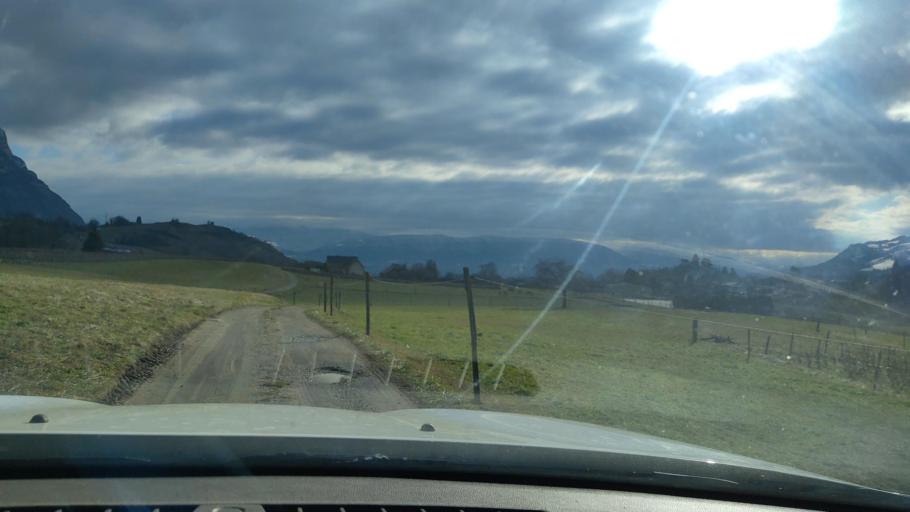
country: FR
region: Rhone-Alpes
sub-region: Departement de la Savoie
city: Challes-les-Eaux
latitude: 45.5368
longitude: 5.9863
